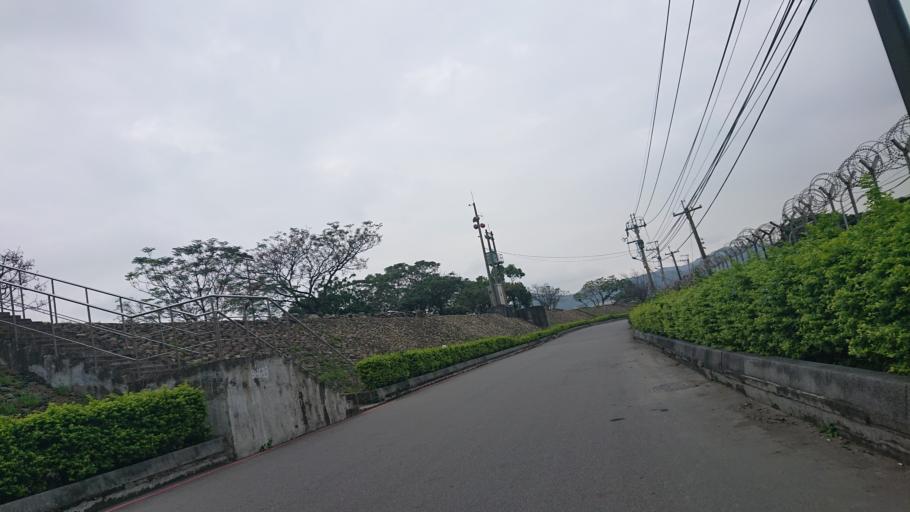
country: TW
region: Taiwan
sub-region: Taoyuan
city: Taoyuan
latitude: 24.9355
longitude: 121.3512
